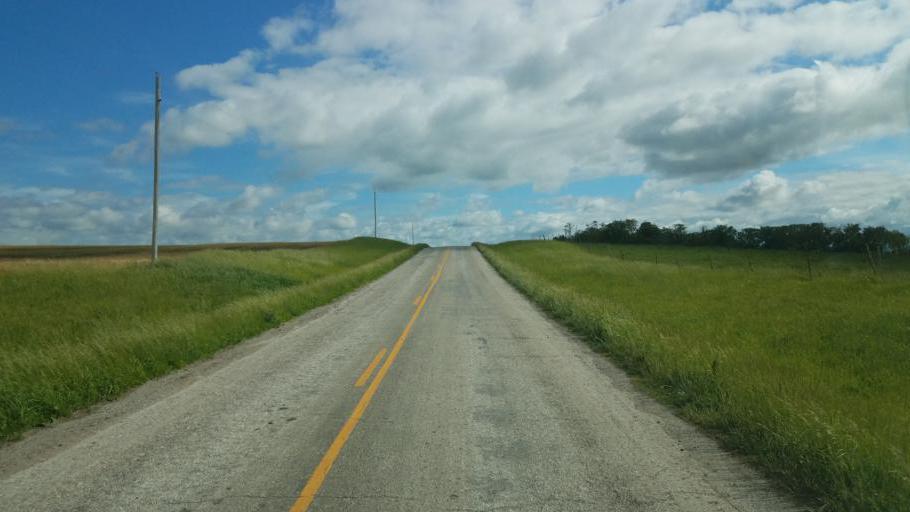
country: US
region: Missouri
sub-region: Mercer County
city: Princeton
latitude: 40.2692
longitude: -93.6757
